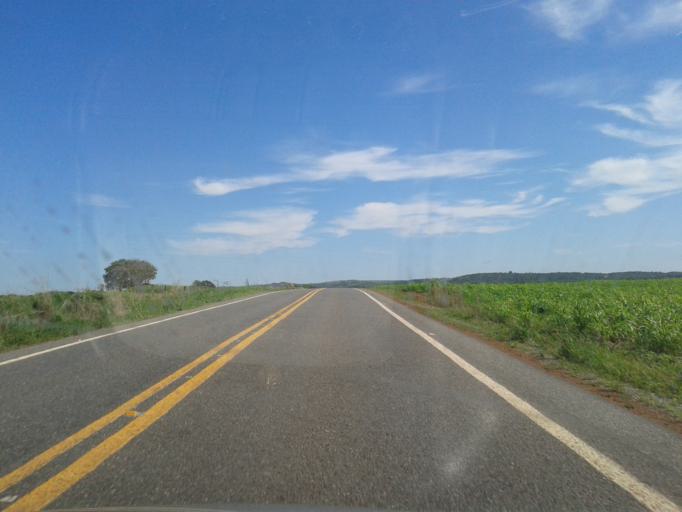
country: BR
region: Goias
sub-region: Piracanjuba
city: Piracanjuba
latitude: -17.3195
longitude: -48.8005
